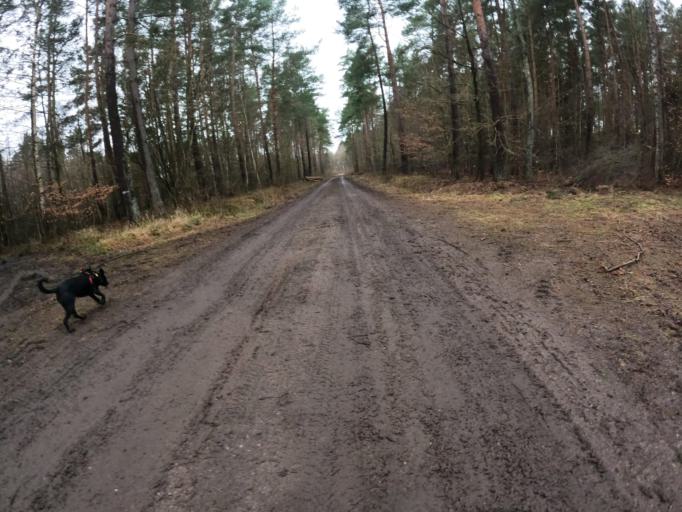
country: PL
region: West Pomeranian Voivodeship
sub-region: Powiat slawienski
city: Darlowo
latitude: 54.4194
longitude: 16.4754
